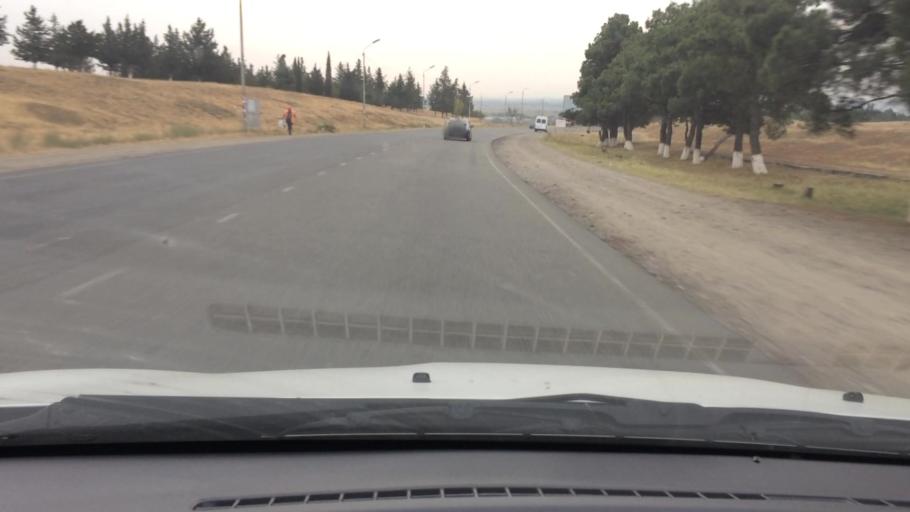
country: GE
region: Kvemo Kartli
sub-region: Marneuli
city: Marneuli
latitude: 41.5036
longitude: 44.8010
